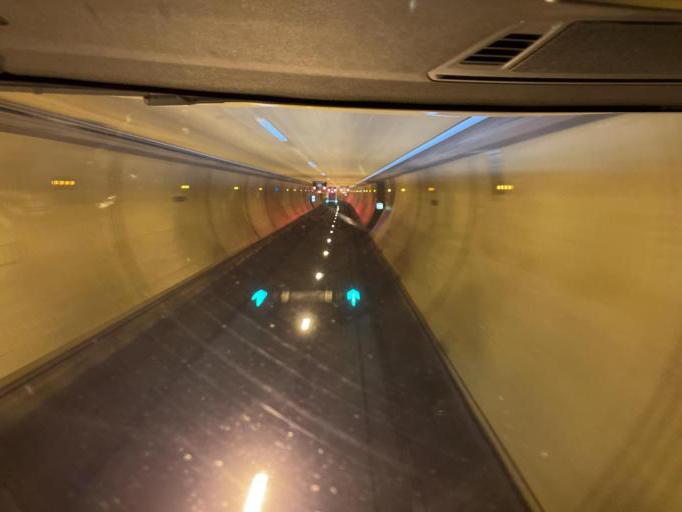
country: FR
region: Provence-Alpes-Cote d'Azur
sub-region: Departement des Alpes-Maritimes
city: Falicon
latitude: 43.7346
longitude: 7.2502
